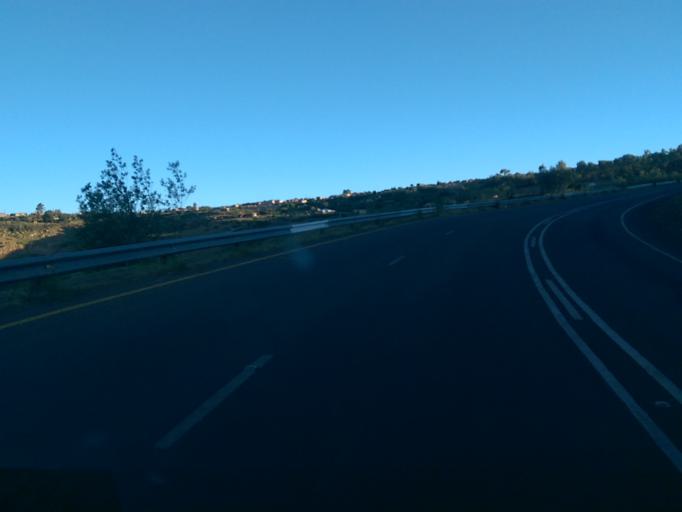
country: LS
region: Maseru
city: Maseru
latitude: -29.4029
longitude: 27.5744
